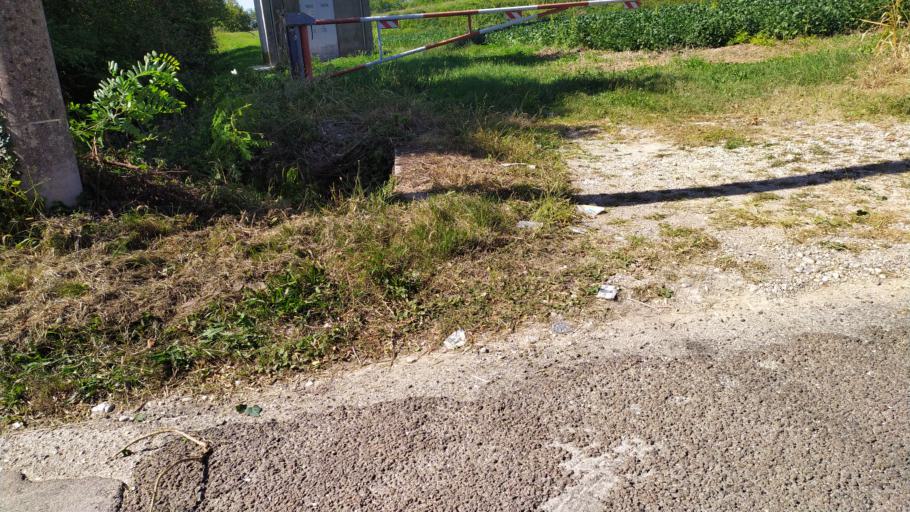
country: IT
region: Friuli Venezia Giulia
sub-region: Provincia di Pordenone
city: Caneva
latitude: 45.9388
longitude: 12.4602
